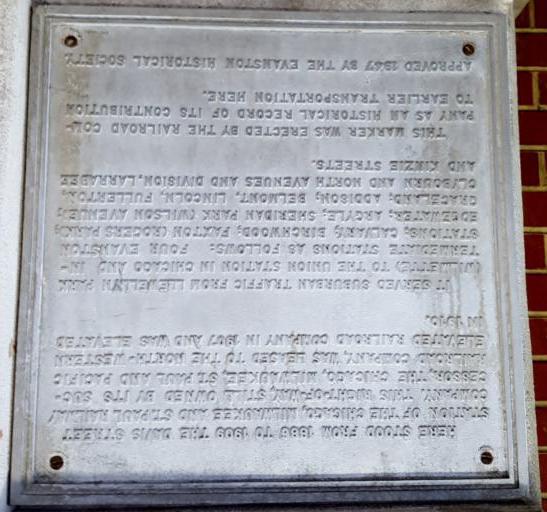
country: US
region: Illinois
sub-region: Cook County
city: Evanston
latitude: 42.0478
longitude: -87.6835
